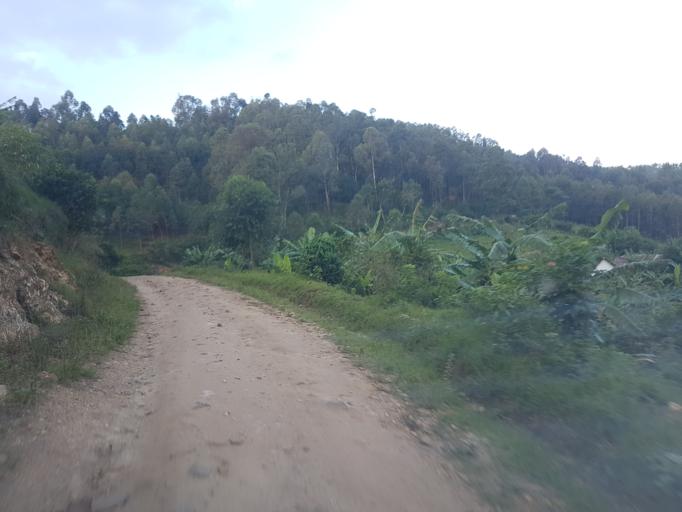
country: UG
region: Western Region
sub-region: Mitoma District
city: Mitoma
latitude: -0.6804
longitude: 29.9151
